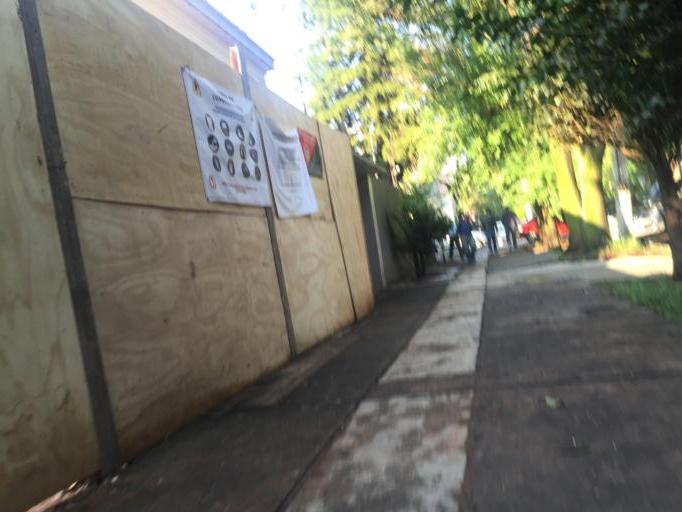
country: MX
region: Mexico City
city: Benito Juarez
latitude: 19.4043
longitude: -99.1663
